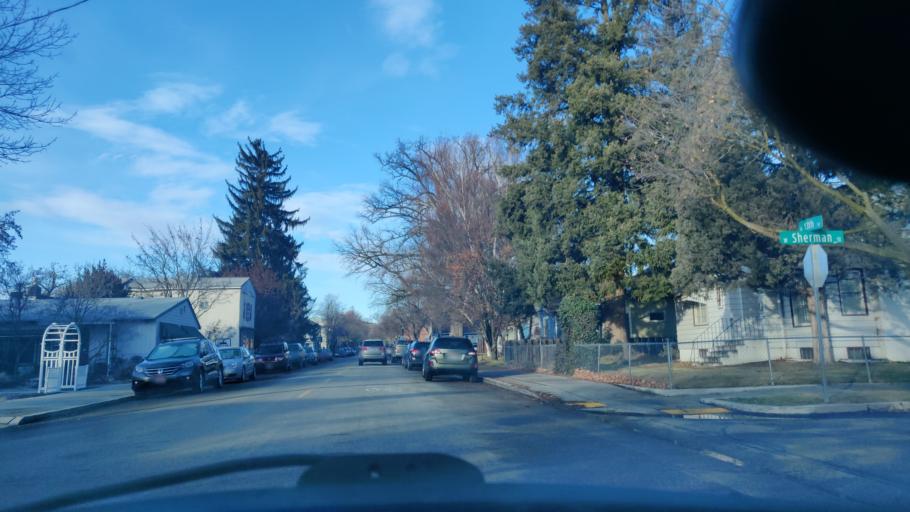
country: US
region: Idaho
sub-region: Ada County
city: Boise
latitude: 43.6283
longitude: -116.2034
